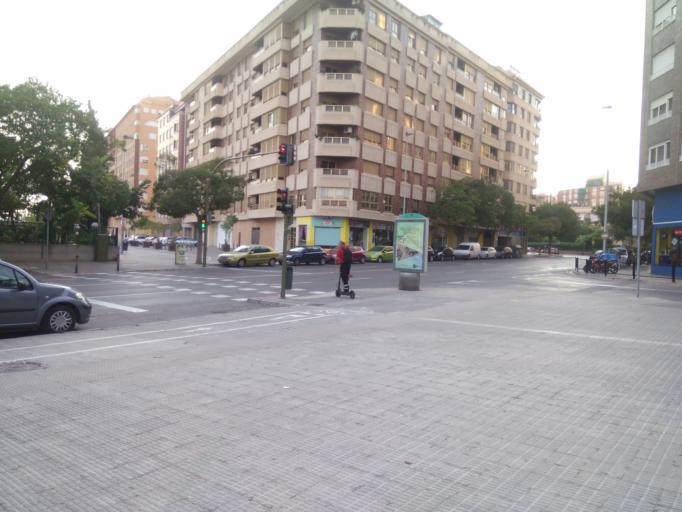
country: ES
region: Valencia
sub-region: Provincia de Castello
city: Castello de la Plana
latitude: 39.9780
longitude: -0.0392
